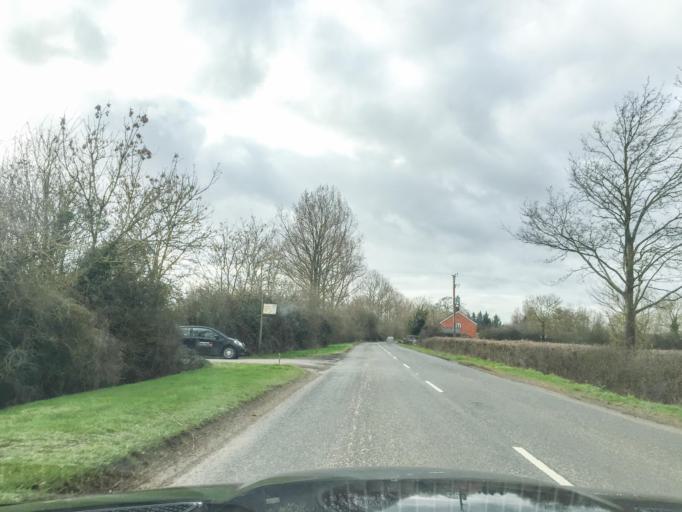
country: GB
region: England
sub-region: Warwickshire
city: Shipston on Stour
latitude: 52.0629
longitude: -1.5847
